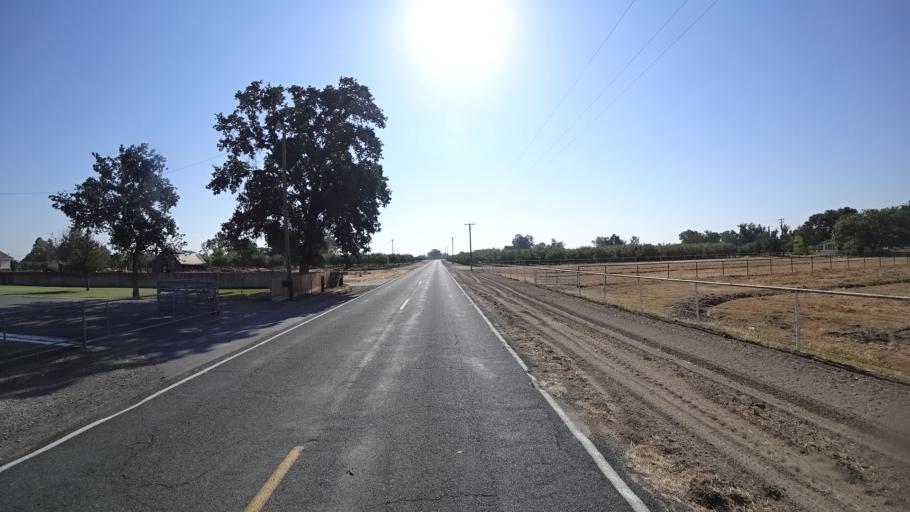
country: US
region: California
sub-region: Fresno County
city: Riverdale
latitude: 36.3658
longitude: -119.8305
